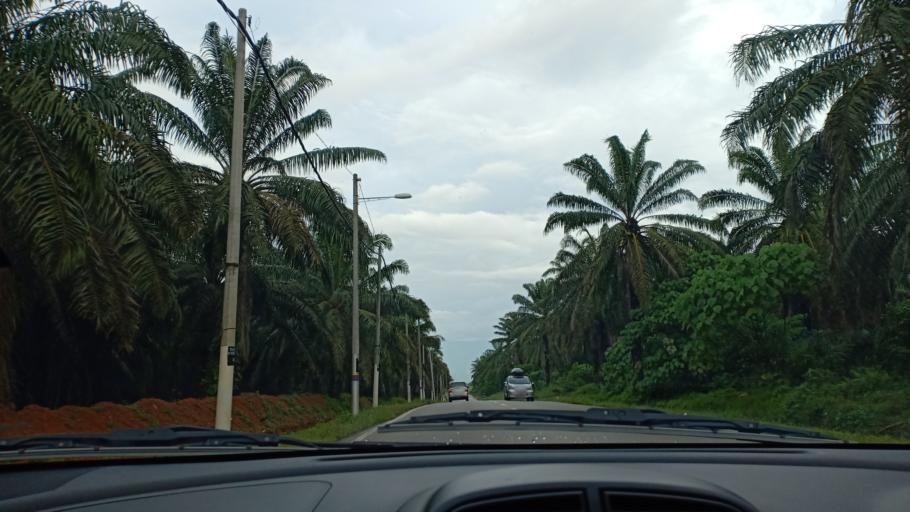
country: MY
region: Penang
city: Tasek Glugor
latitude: 5.4477
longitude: 100.4846
